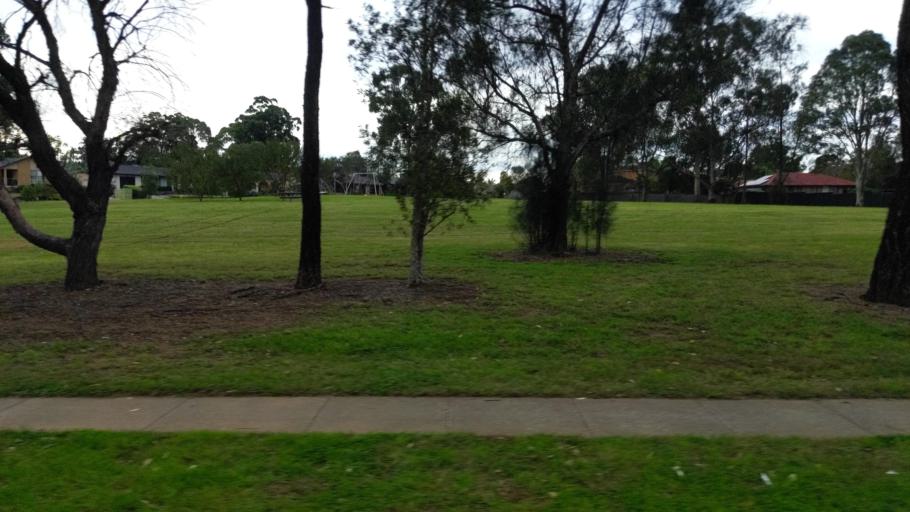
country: AU
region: New South Wales
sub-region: Blacktown
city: Blacktown
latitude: -33.7541
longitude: 150.9405
